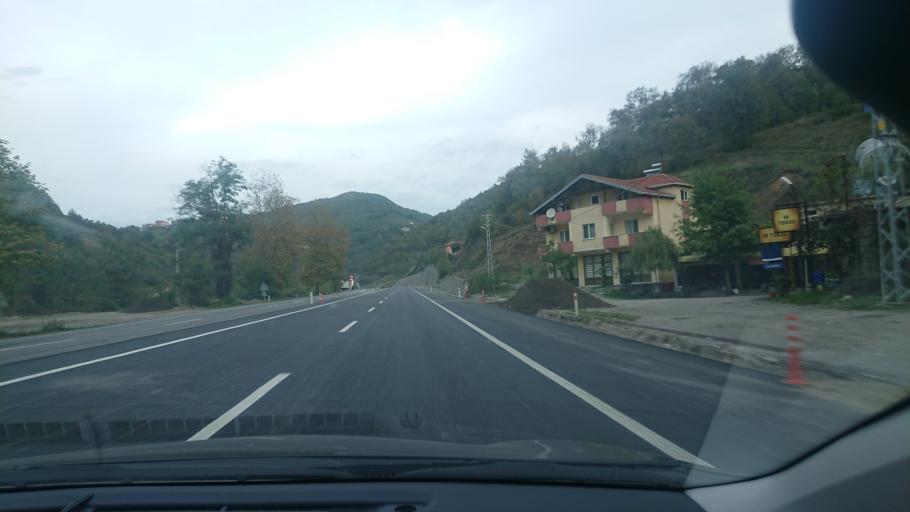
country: TR
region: Zonguldak
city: Beycuma
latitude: 41.3832
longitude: 31.9436
